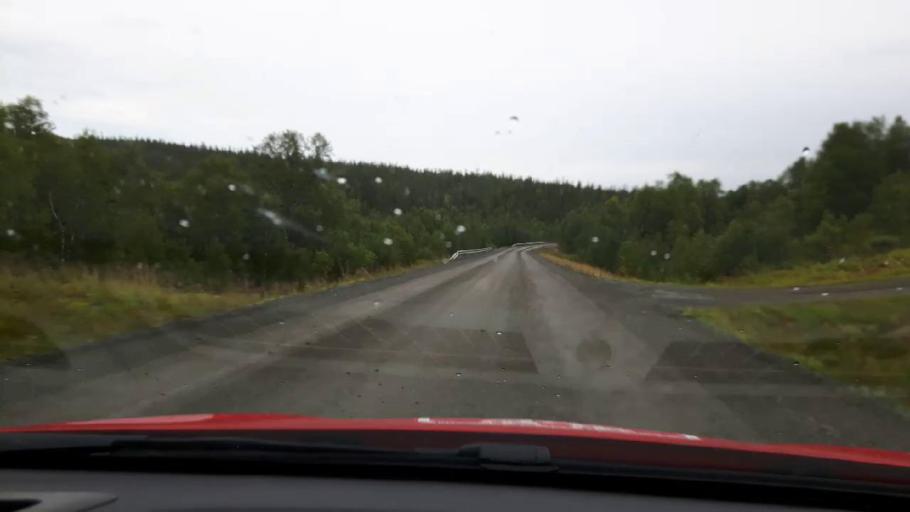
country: NO
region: Nord-Trondelag
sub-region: Meraker
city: Meraker
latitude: 63.5780
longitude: 12.2752
